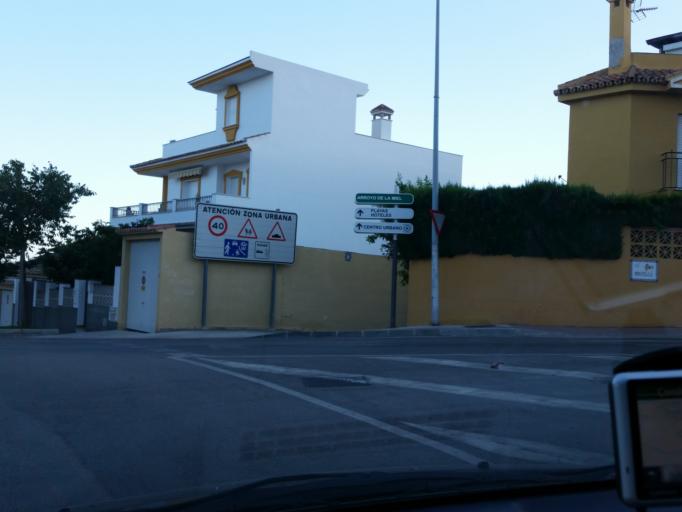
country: ES
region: Andalusia
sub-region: Provincia de Malaga
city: Benalmadena
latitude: 36.6069
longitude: -4.5342
